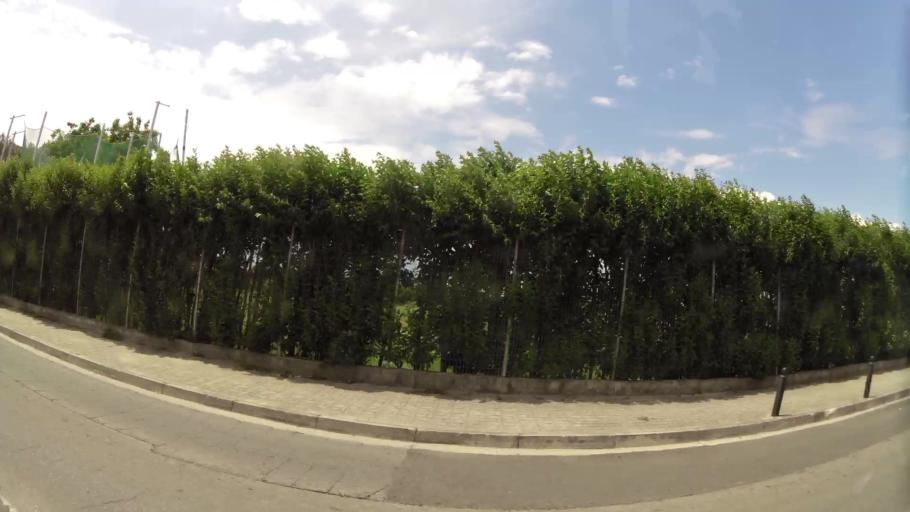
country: GR
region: Central Macedonia
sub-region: Nomos Pierias
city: Katerini
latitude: 40.2605
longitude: 22.5122
